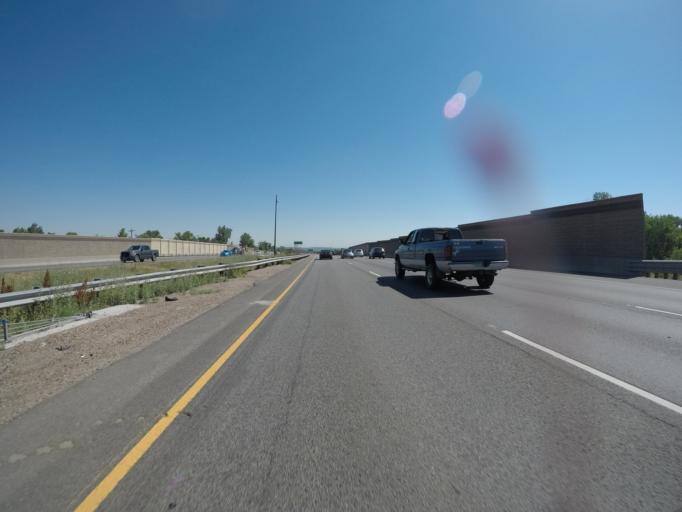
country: US
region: Colorado
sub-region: Jefferson County
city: Applewood
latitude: 39.7466
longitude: -105.1514
